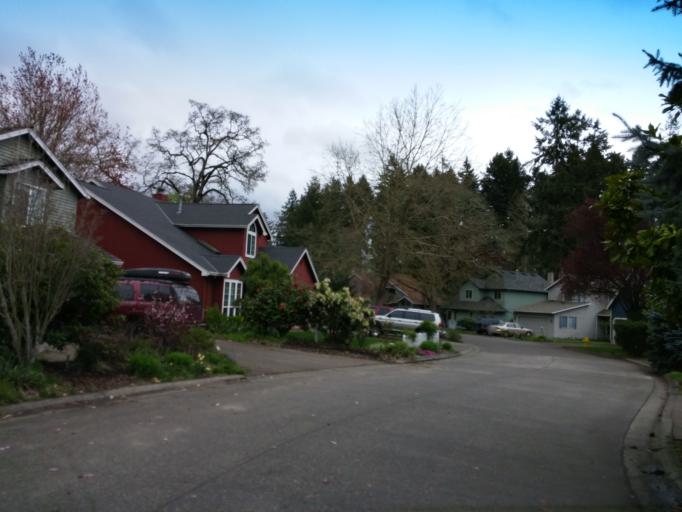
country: US
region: Oregon
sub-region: Washington County
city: Oak Hills
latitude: 45.5282
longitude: -122.8542
